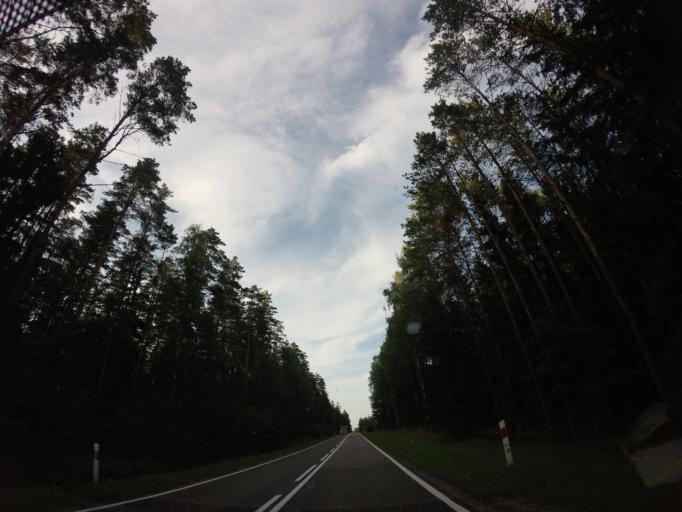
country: PL
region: Podlasie
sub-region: Powiat sejnenski
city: Sejny
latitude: 53.9921
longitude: 23.3058
